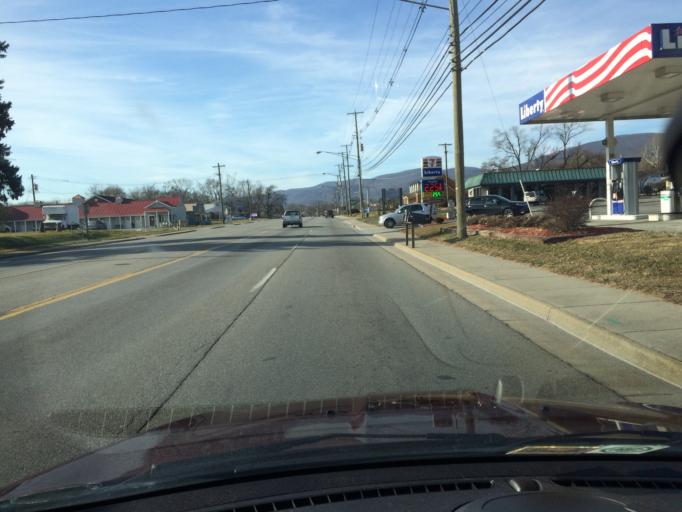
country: US
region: Virginia
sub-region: City of Salem
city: Salem
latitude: 37.2819
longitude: -80.1065
